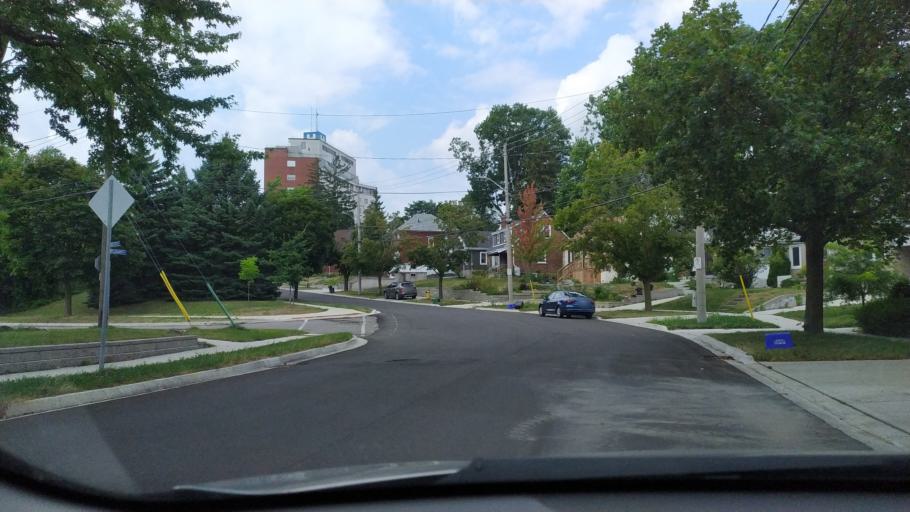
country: CA
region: Ontario
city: Kitchener
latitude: 43.4373
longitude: -80.4983
